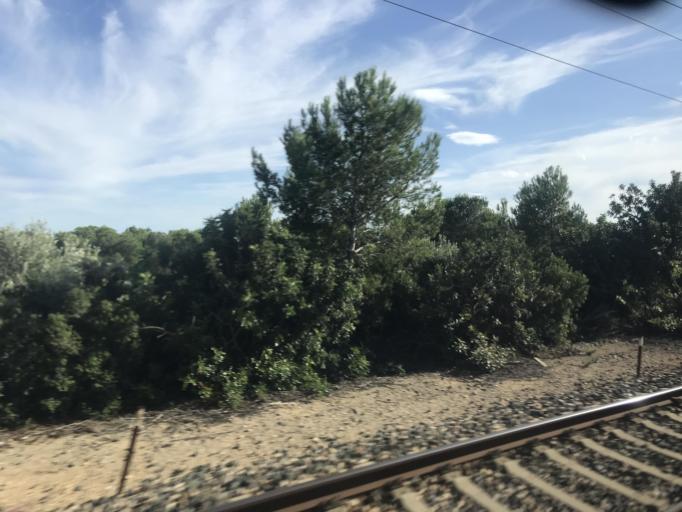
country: ES
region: Catalonia
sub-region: Provincia de Tarragona
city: El Perello
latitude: 40.8540
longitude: 0.7639
